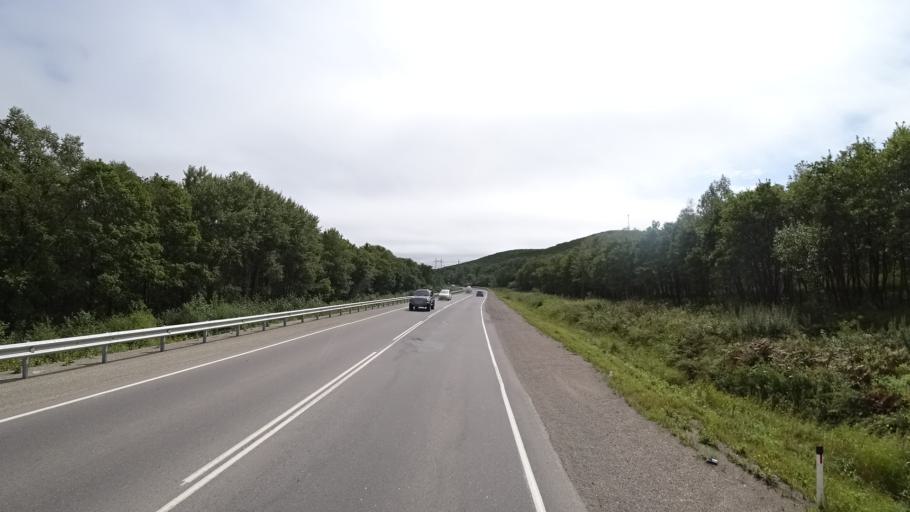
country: RU
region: Primorskiy
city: Lyalichi
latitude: 44.1118
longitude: 132.4201
